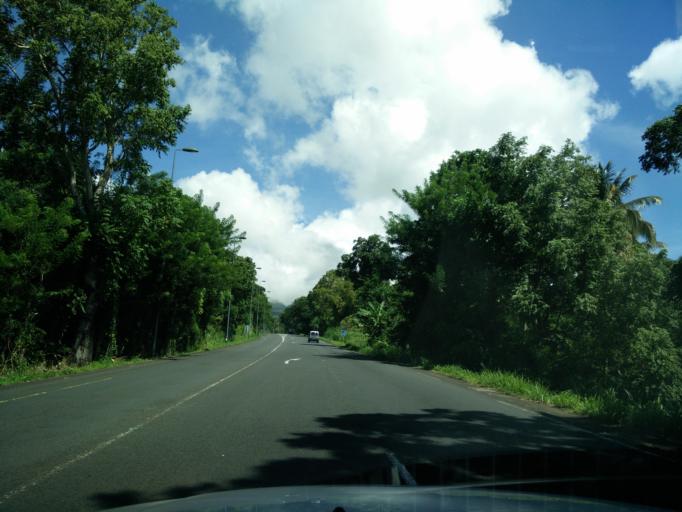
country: GP
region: Guadeloupe
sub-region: Guadeloupe
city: Gourbeyre
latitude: 15.9974
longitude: -61.7037
